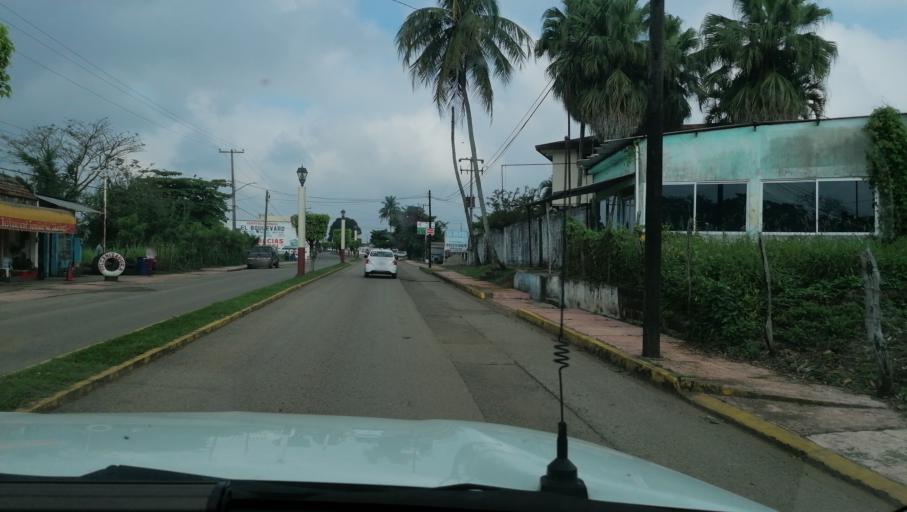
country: MX
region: Chiapas
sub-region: Juarez
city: El Triunfo 1ra. Seccion (Cardona)
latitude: 17.6030
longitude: -93.1857
